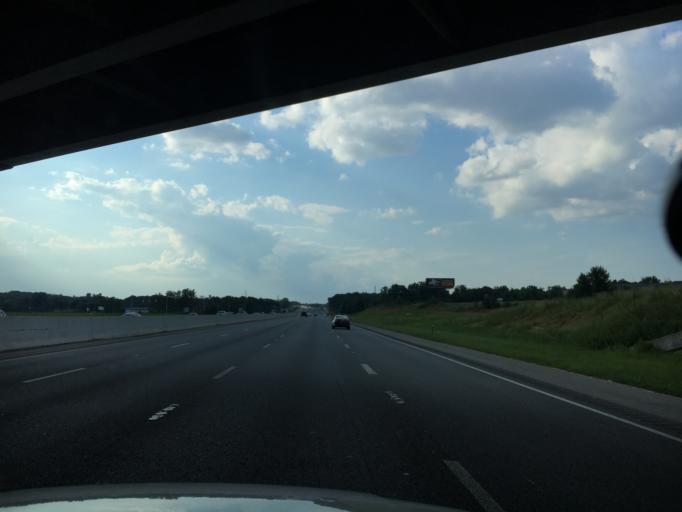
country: US
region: South Carolina
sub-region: Greenville County
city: Simpsonville
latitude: 34.7373
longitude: -82.2714
